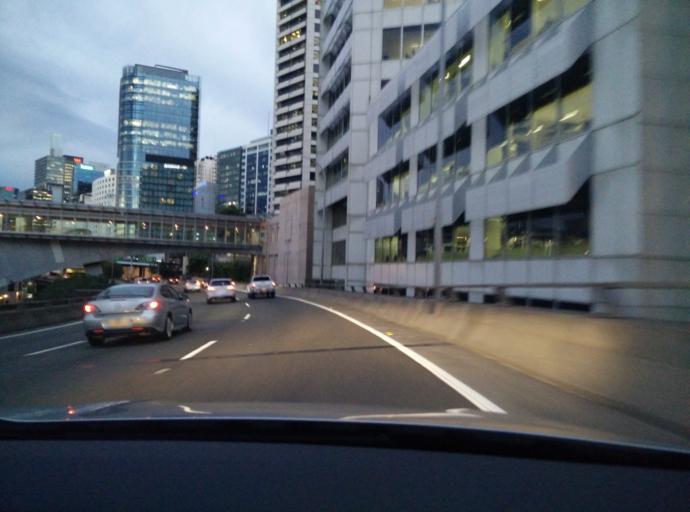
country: AU
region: New South Wales
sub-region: City of Sydney
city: Haymarket
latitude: -33.8729
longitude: 151.2024
